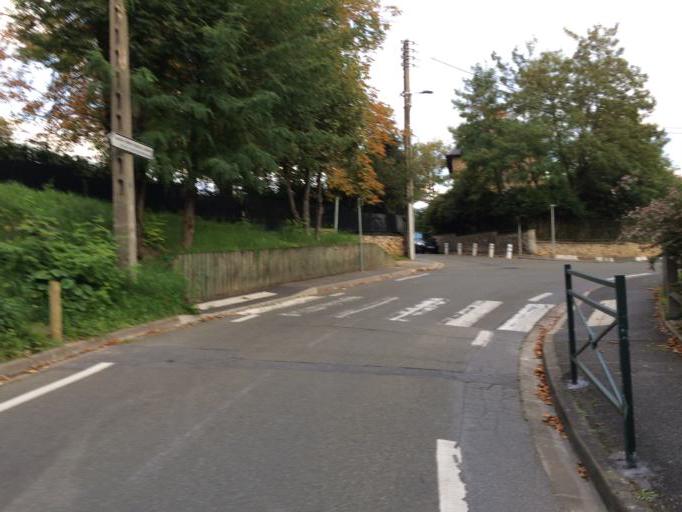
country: FR
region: Ile-de-France
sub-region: Departement de l'Essonne
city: Orsay
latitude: 48.7064
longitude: 2.2120
